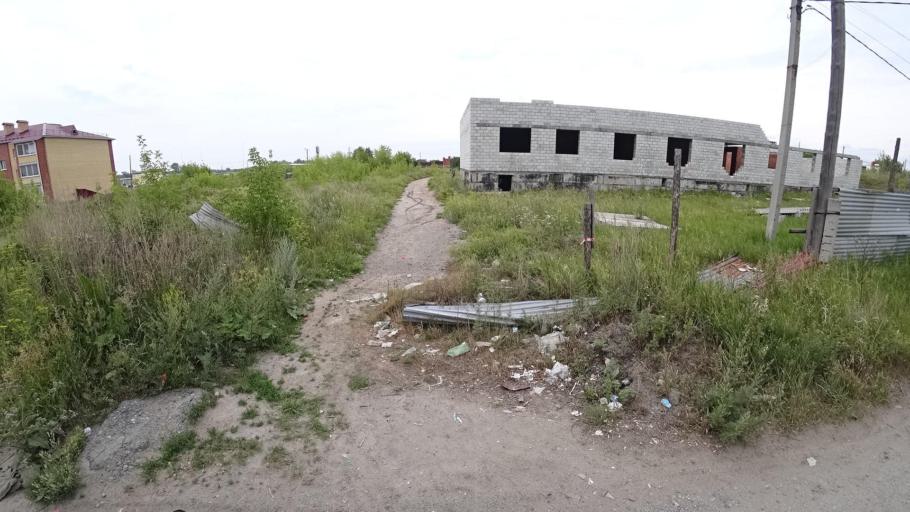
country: RU
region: Sverdlovsk
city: Kamyshlov
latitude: 56.8460
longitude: 62.7426
